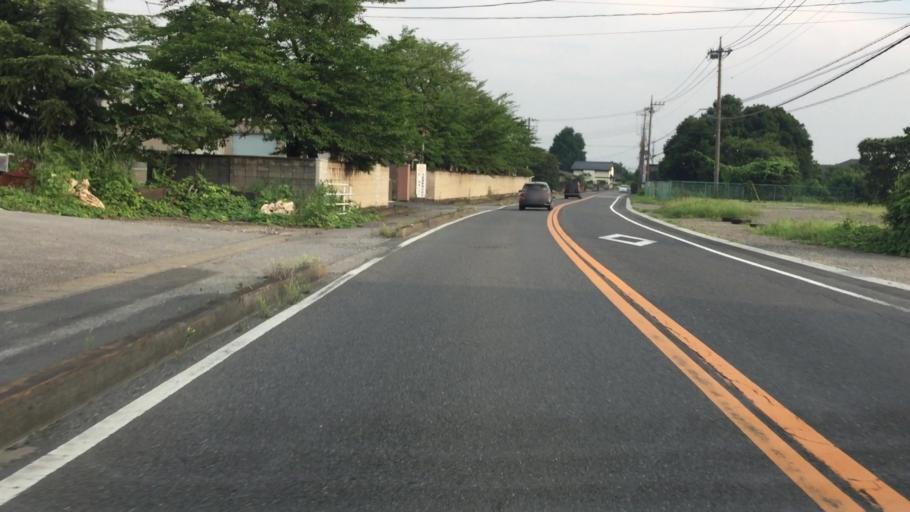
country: JP
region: Tochigi
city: Fujioka
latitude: 36.3104
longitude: 139.6724
